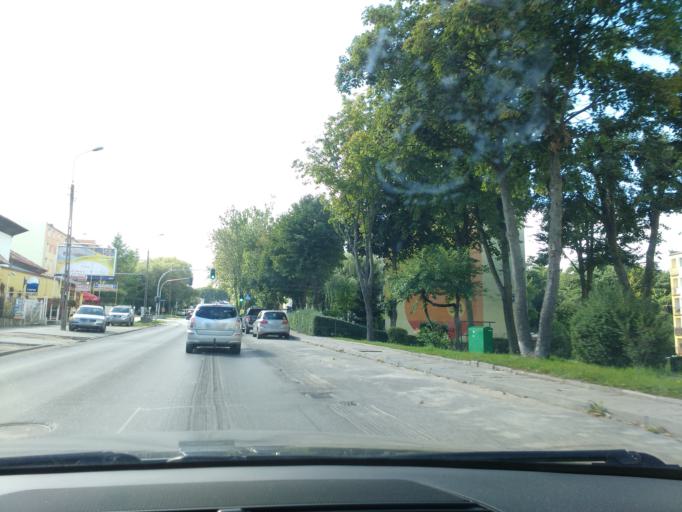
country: PL
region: Pomeranian Voivodeship
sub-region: Gdynia
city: Wielki Kack
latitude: 54.4985
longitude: 18.5015
